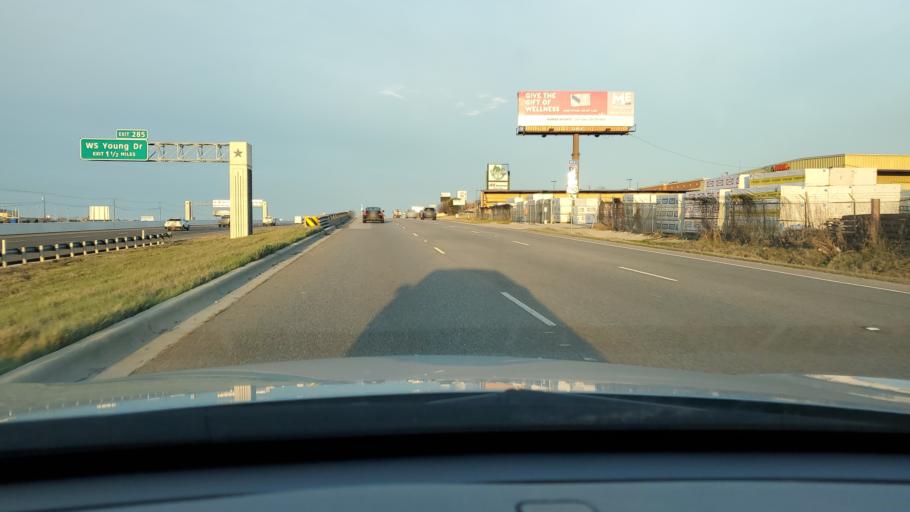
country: US
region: Texas
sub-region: Bell County
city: Harker Heights
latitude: 31.0736
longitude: -97.6788
